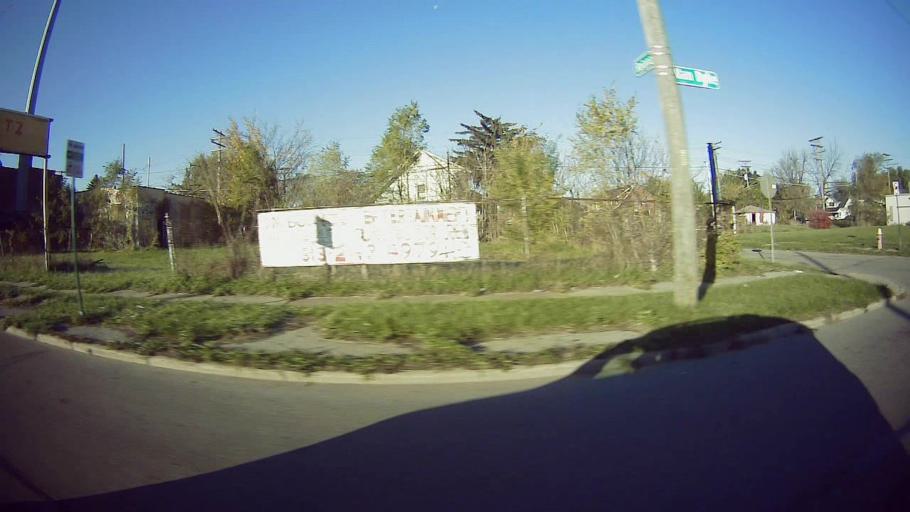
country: US
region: Michigan
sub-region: Wayne County
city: Hamtramck
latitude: 42.3971
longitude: -83.0230
